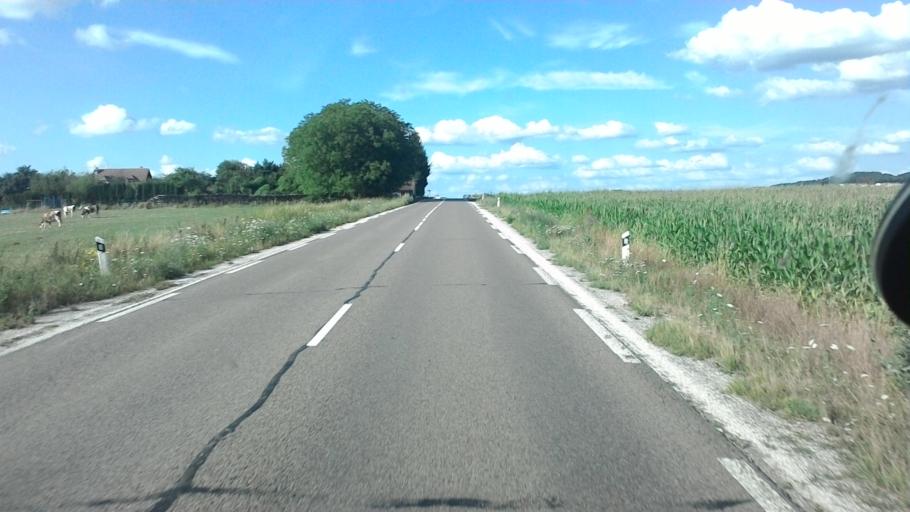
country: FR
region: Franche-Comte
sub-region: Departement de la Haute-Saone
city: Luxeuil-les-Bains
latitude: 47.7200
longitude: 6.3044
